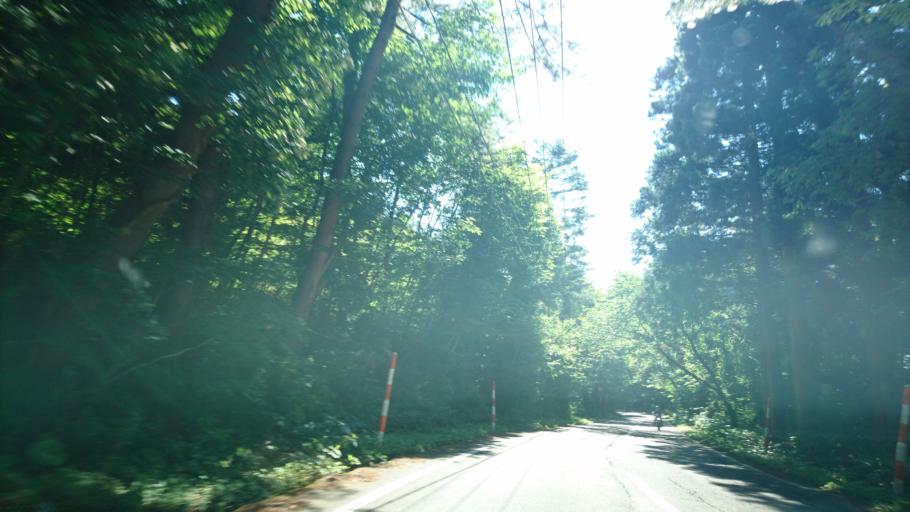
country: JP
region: Akita
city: Kakunodatemachi
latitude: 39.7512
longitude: 140.6538
